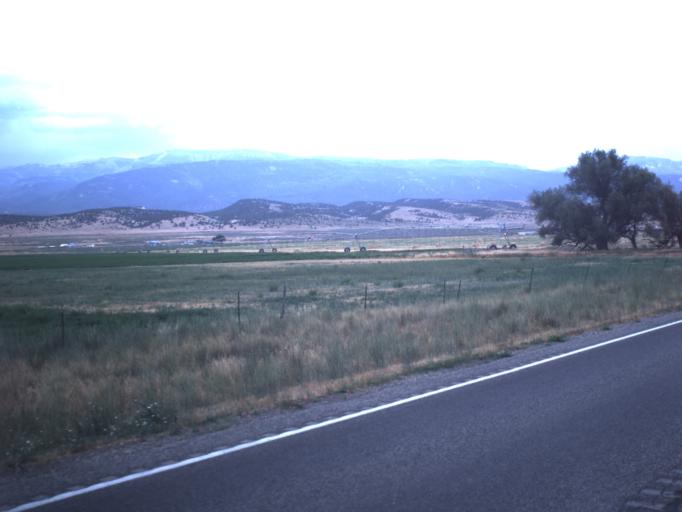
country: US
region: Utah
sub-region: Sanpete County
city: Moroni
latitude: 39.4699
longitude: -111.5628
